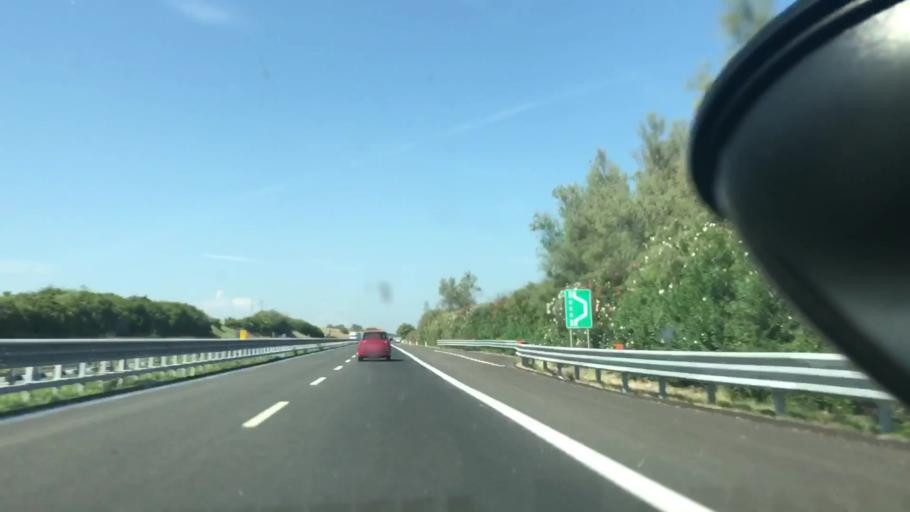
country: IT
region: Molise
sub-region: Provincia di Campobasso
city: Petacciato
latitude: 42.0193
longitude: 14.8960
